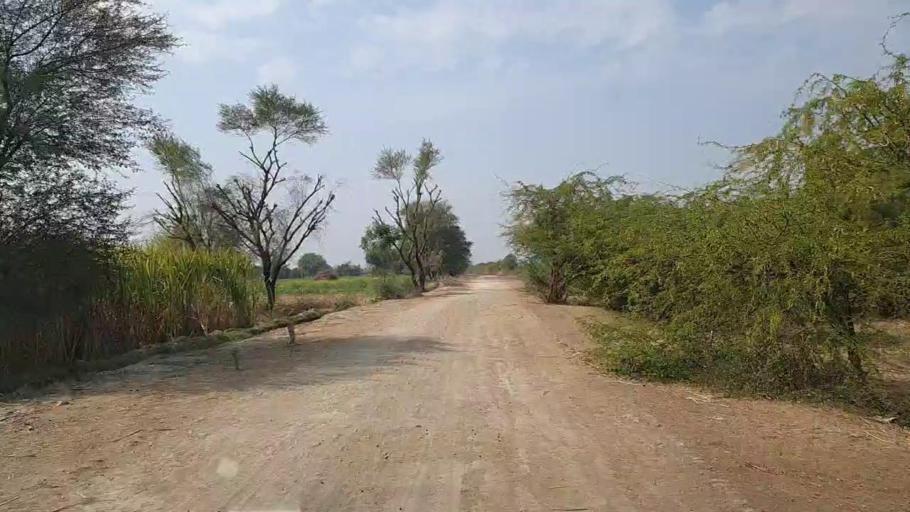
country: PK
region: Sindh
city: Mirwah Gorchani
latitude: 25.3490
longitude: 69.0711
